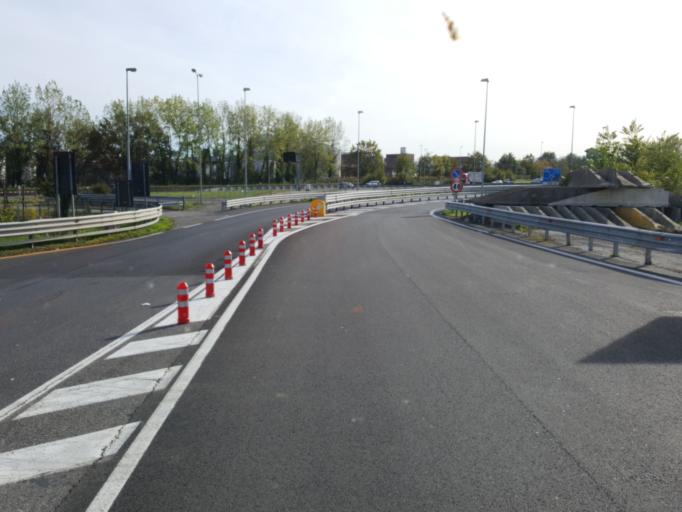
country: IT
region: Emilia-Romagna
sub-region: Provincia di Ravenna
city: Faenza
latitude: 44.3219
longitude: 11.9039
